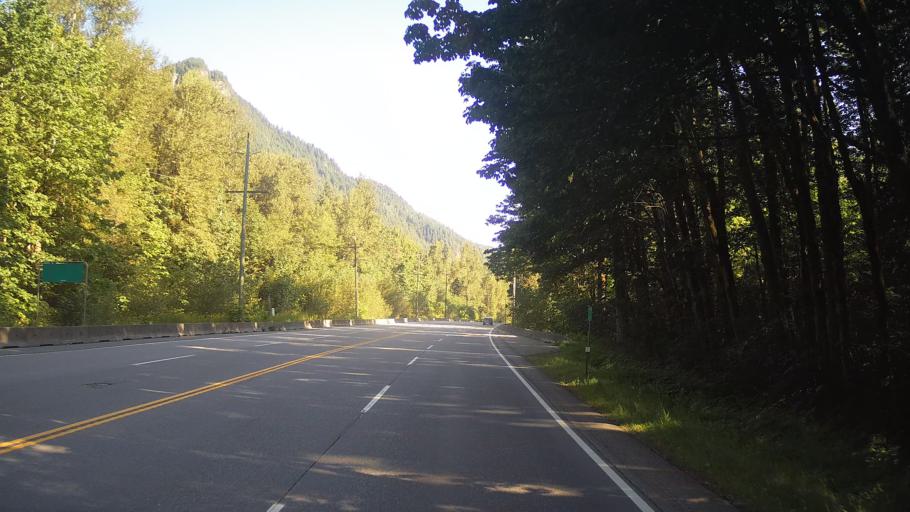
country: CA
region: British Columbia
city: Hope
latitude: 49.4471
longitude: -121.4373
